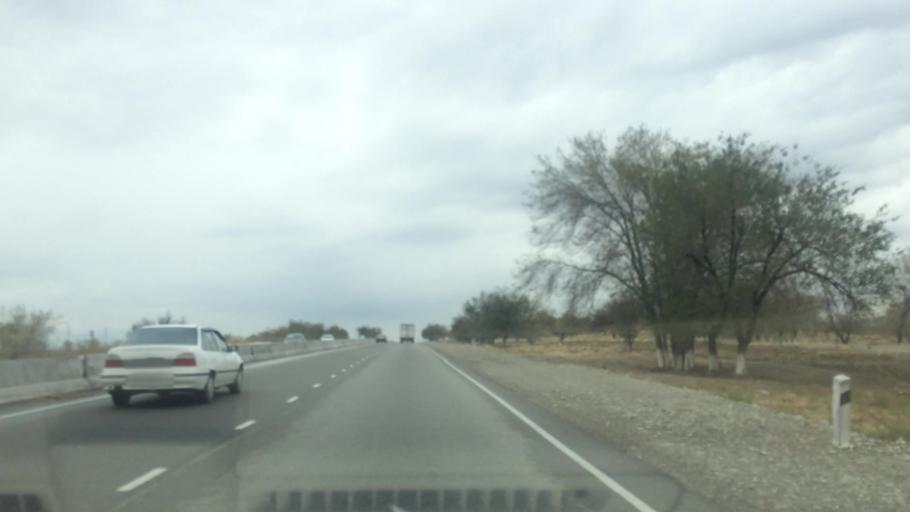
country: UZ
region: Samarqand
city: Bulung'ur
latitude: 39.9302
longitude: 67.5216
